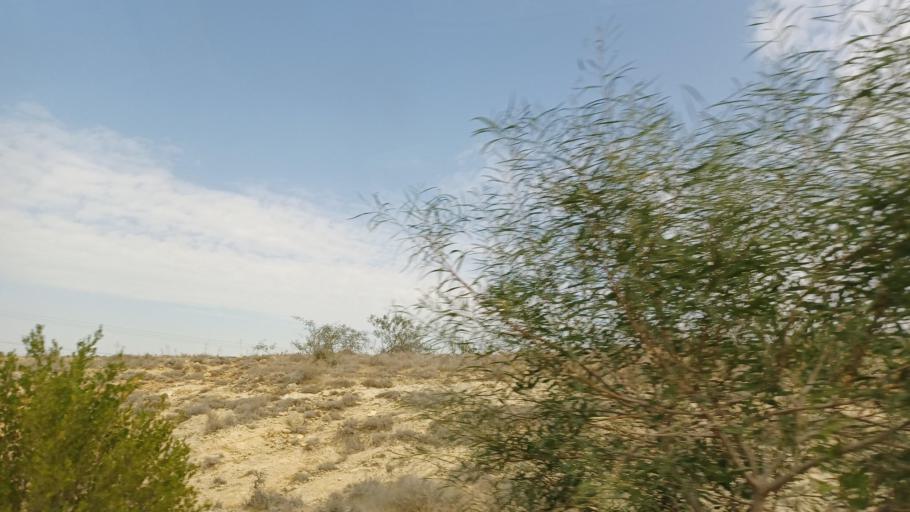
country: CY
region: Lefkosia
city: Meniko
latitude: 35.0641
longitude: 33.1250
